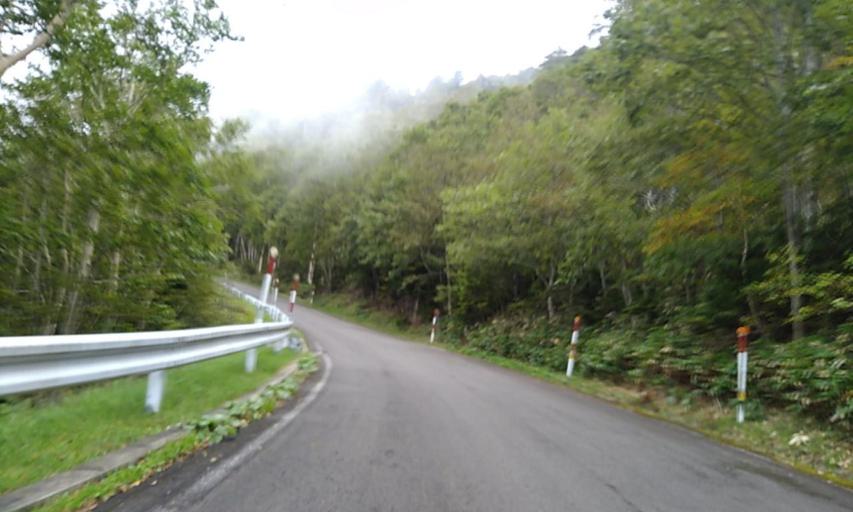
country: JP
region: Hokkaido
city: Bihoro
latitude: 43.5741
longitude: 144.2368
